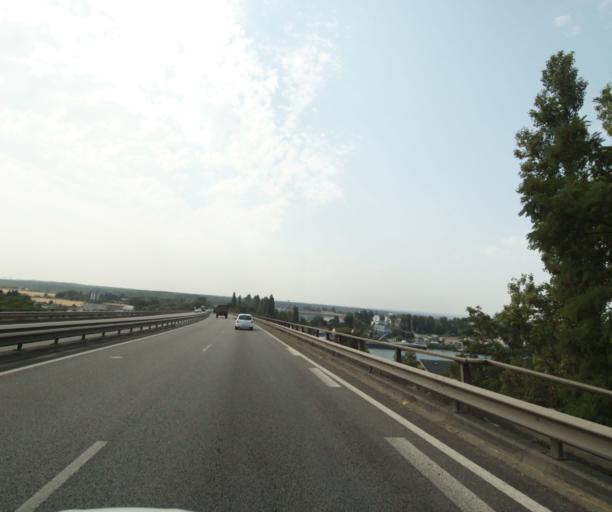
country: FR
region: Ile-de-France
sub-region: Departement des Yvelines
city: Conflans-Sainte-Honorine
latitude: 48.9904
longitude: 2.0816
